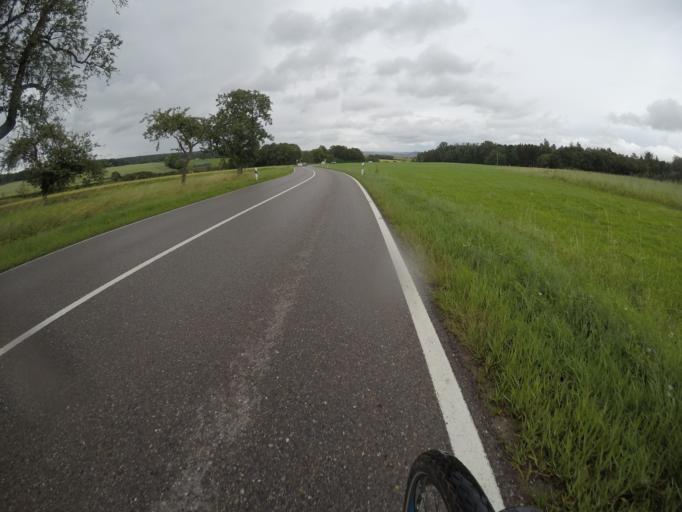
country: DE
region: Baden-Wuerttemberg
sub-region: Regierungsbezirk Stuttgart
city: Unterjettingen
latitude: 48.5721
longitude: 8.8156
